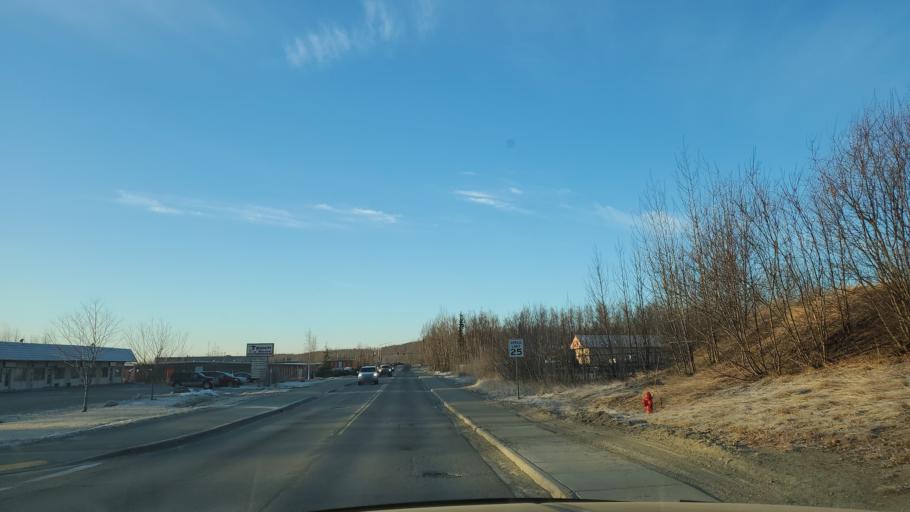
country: US
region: Alaska
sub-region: Matanuska-Susitna Borough
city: Wasilla
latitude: 61.5850
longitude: -149.4435
